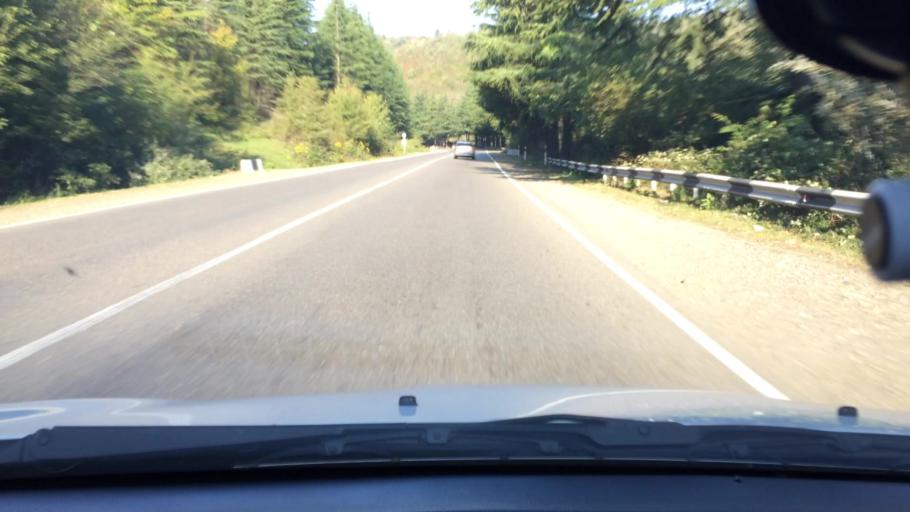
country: GE
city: Shorapani
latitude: 42.0939
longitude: 43.1128
